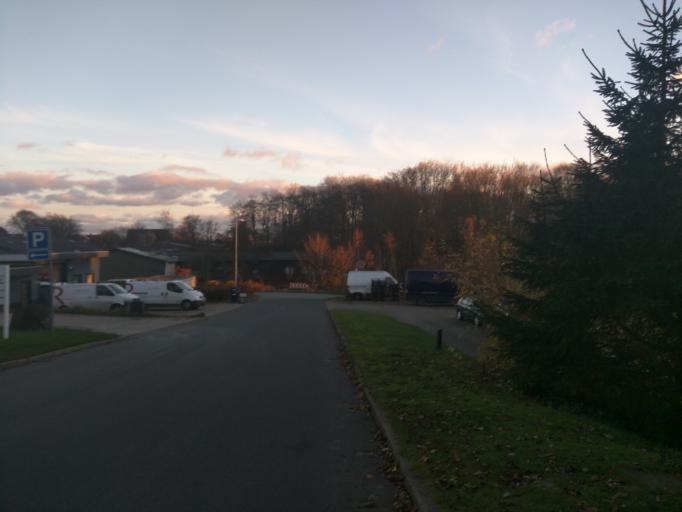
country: DK
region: Central Jutland
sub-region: Skanderborg Kommune
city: Horning
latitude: 56.0808
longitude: 10.0325
